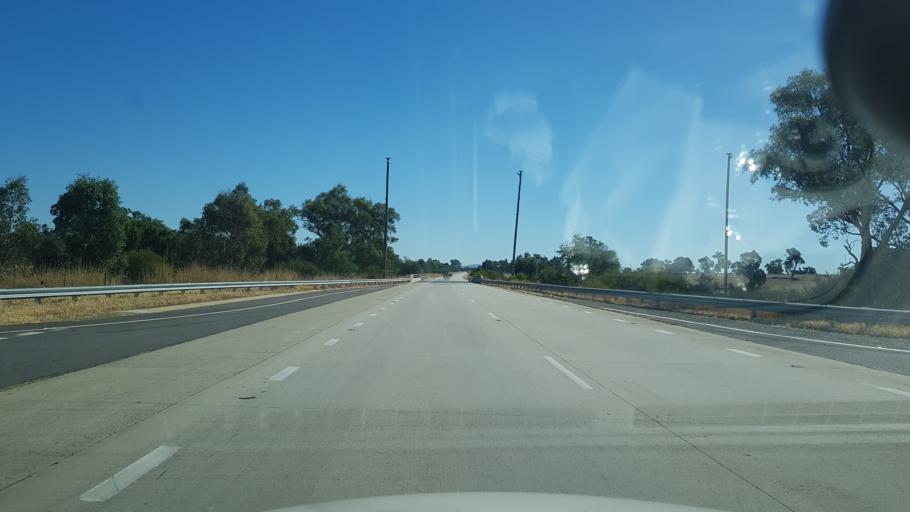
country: AU
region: New South Wales
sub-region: Greater Hume Shire
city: Jindera
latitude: -35.9253
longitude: 147.0333
